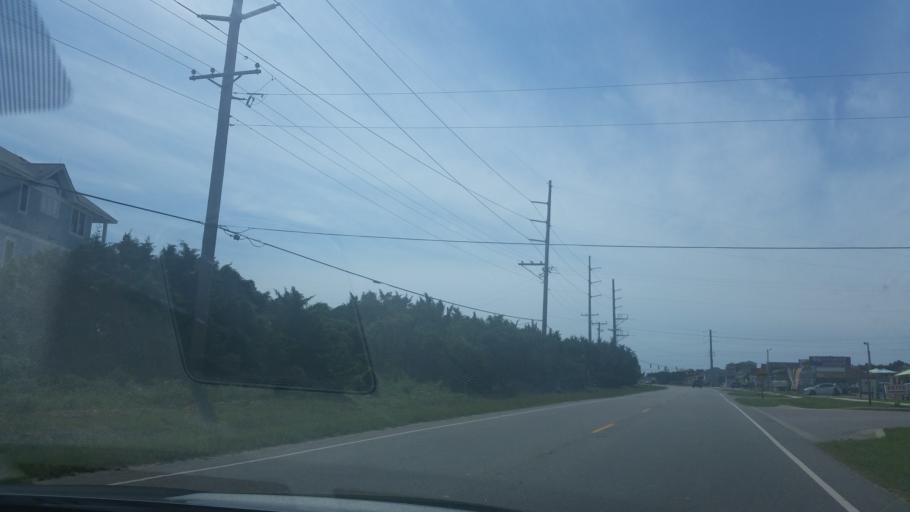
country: US
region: North Carolina
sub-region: Dare County
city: Buxton
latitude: 35.3547
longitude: -75.5028
